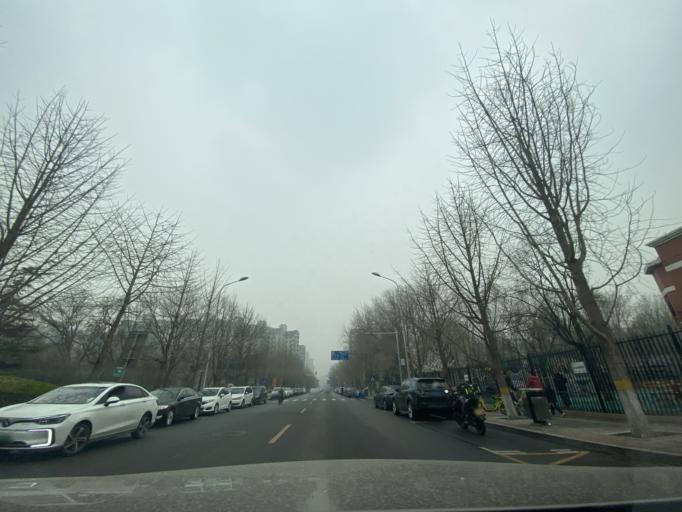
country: CN
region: Beijing
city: Sijiqing
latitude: 39.9639
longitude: 116.2739
